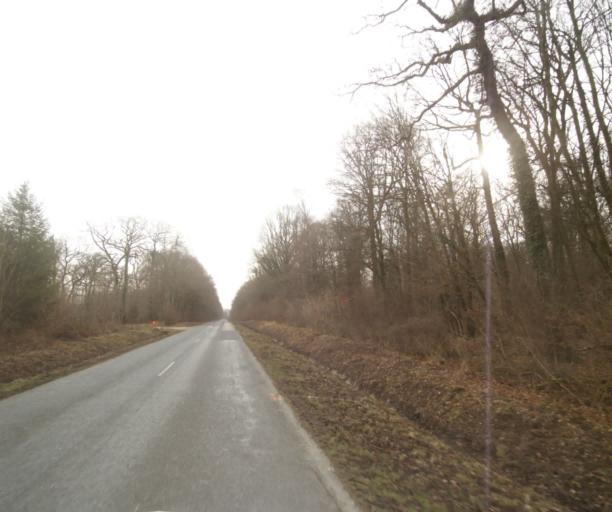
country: FR
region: Champagne-Ardenne
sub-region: Departement de la Haute-Marne
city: Villiers-en-Lieu
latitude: 48.7136
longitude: 4.8845
